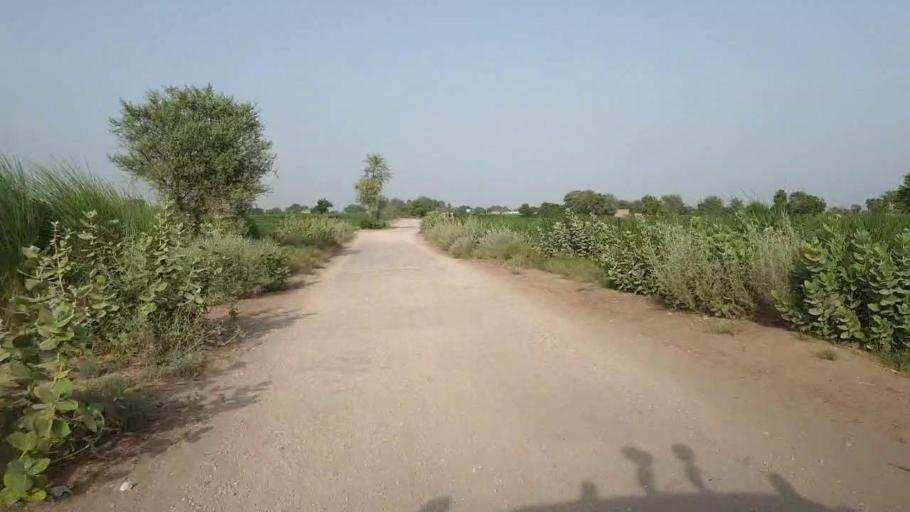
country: PK
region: Sindh
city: Daur
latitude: 26.3430
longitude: 68.2781
